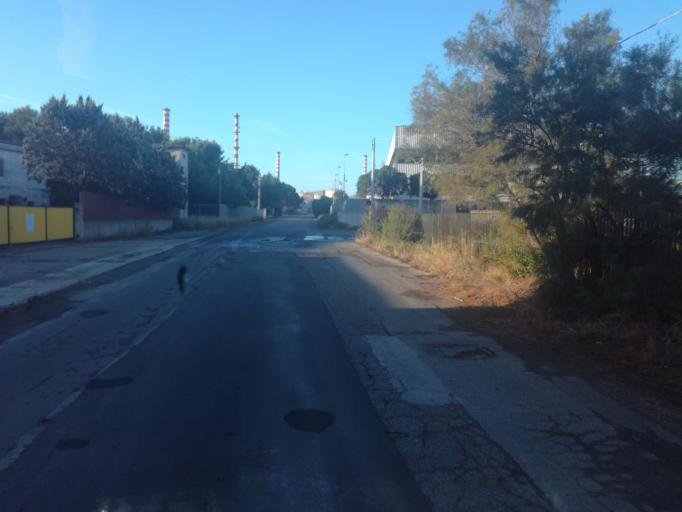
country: IT
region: Apulia
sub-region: Provincia di Taranto
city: Statte
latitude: 40.4989
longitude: 17.1981
